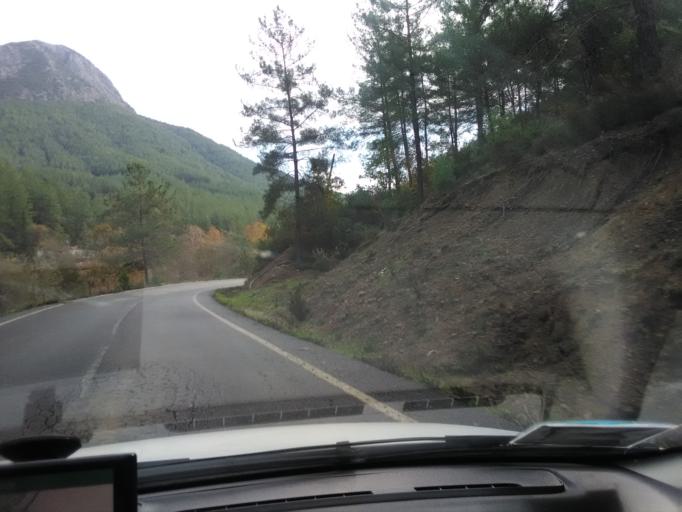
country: TR
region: Antalya
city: Gazipasa
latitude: 36.2467
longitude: 32.4107
